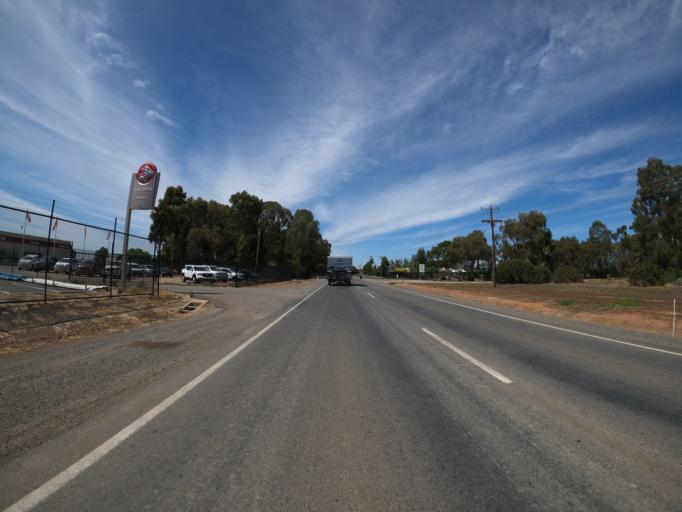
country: AU
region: Victoria
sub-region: Moira
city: Yarrawonga
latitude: -36.0310
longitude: 145.9955
